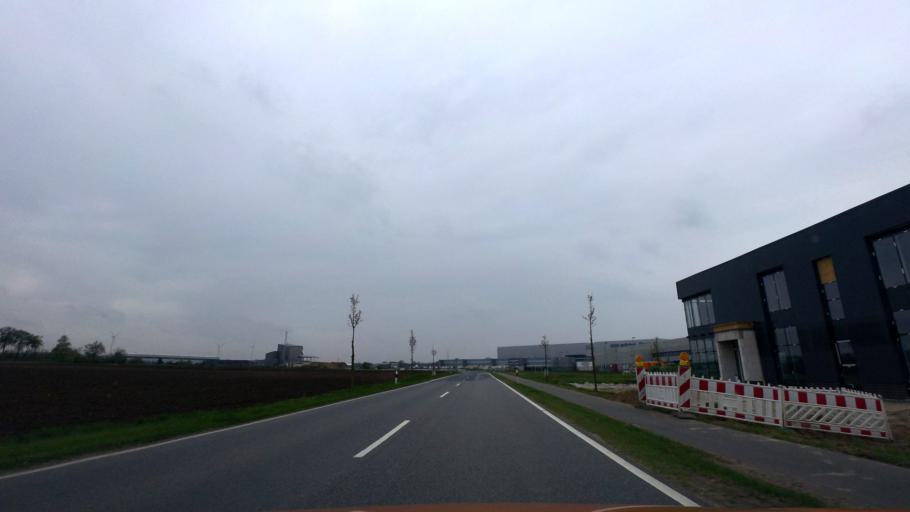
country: DE
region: Lower Saxony
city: Neuenkirchen
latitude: 52.4884
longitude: 8.0599
